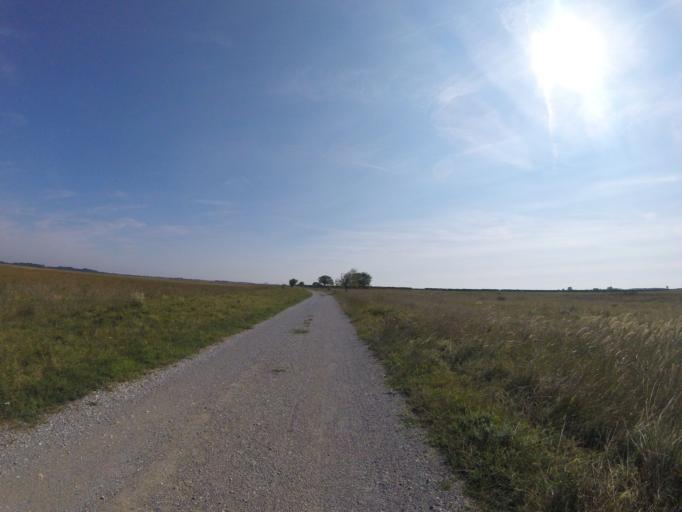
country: AT
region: Burgenland
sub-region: Politischer Bezirk Neusiedl am See
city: Apetlon
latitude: 47.7562
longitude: 16.8585
